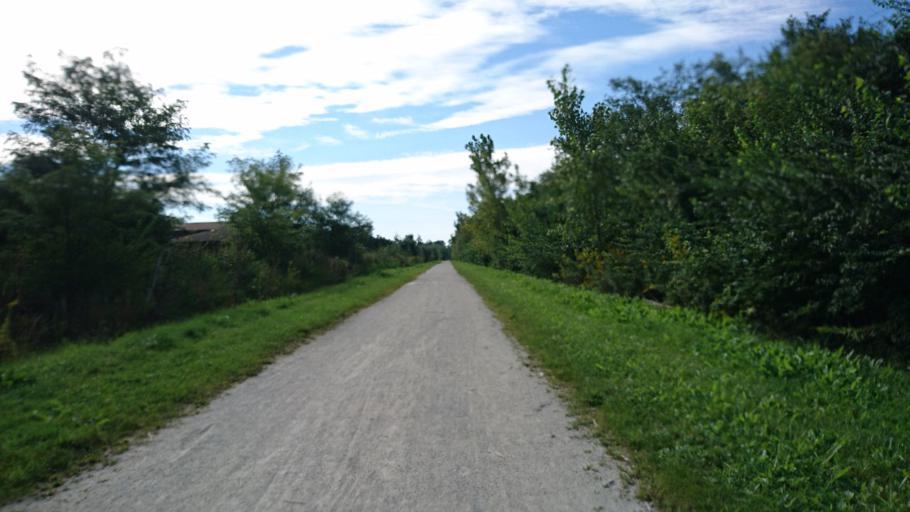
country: US
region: Illinois
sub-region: Will County
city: Manhattan
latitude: 41.4294
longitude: -87.9975
